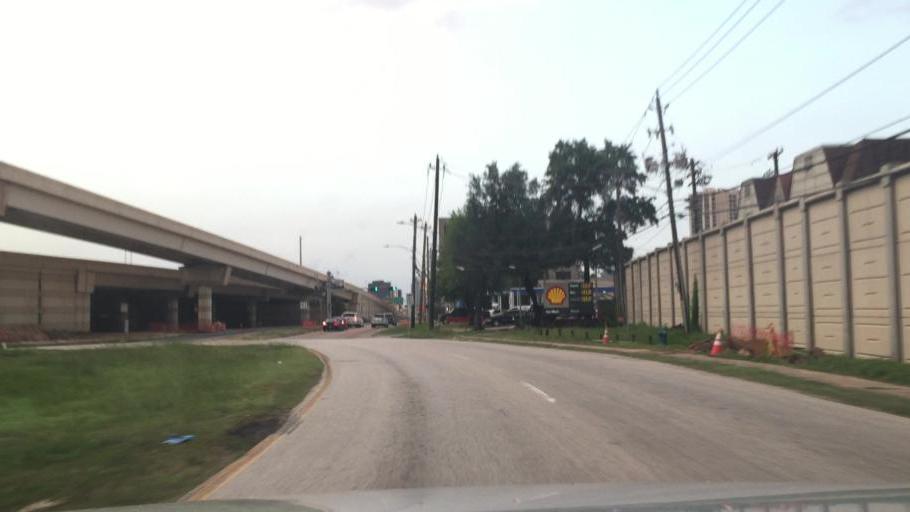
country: US
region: Texas
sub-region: Harris County
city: Hunters Creek Village
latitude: 29.7745
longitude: -95.4568
